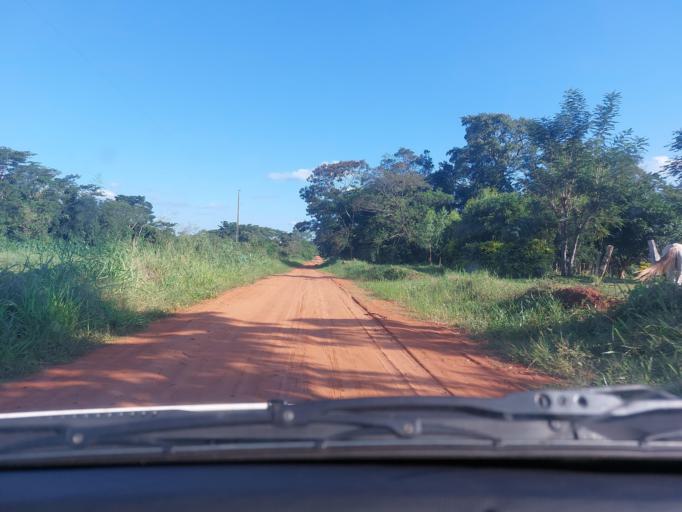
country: PY
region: San Pedro
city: Itacurubi del Rosario
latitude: -24.5367
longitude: -56.5657
